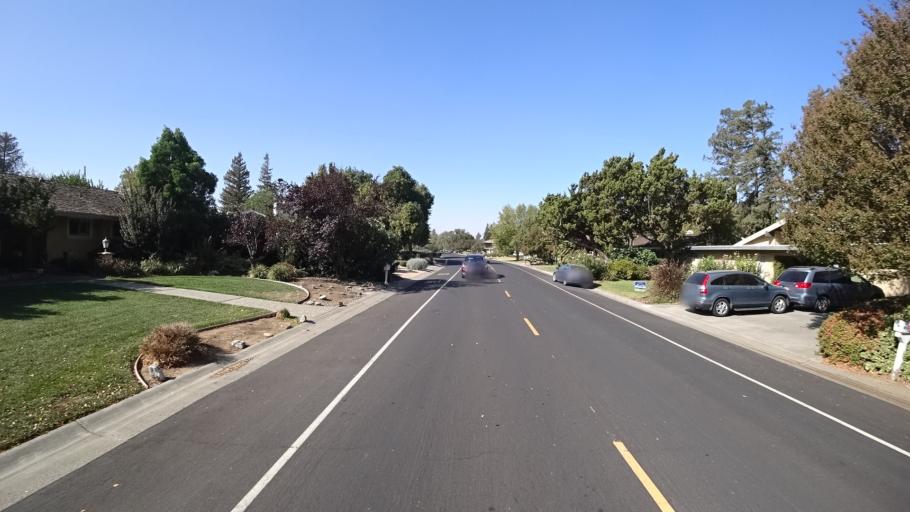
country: US
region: California
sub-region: Yolo County
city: Davis
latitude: 38.5478
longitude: -121.6879
